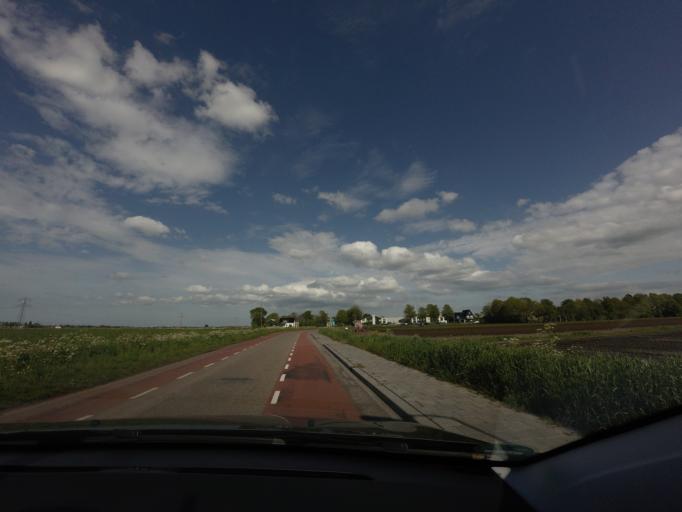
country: NL
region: North Holland
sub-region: Gemeente Heerhugowaard
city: Heerhugowaard
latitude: 52.6347
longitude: 4.8893
